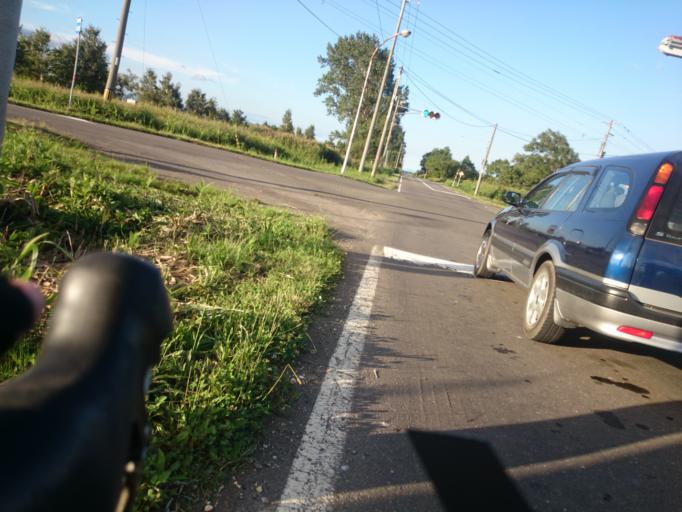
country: JP
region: Hokkaido
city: Tobetsu
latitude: 43.2093
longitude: 141.5858
